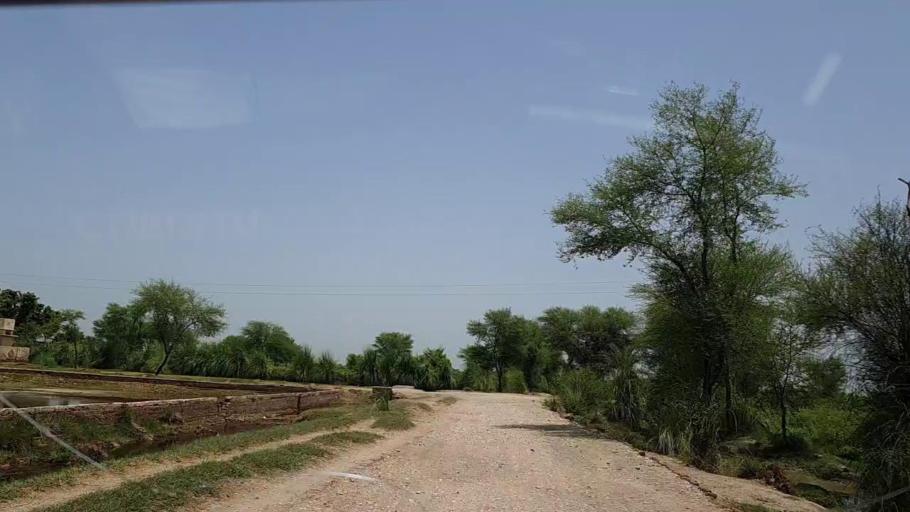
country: PK
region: Sindh
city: Tharu Shah
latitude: 26.9260
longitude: 68.0412
